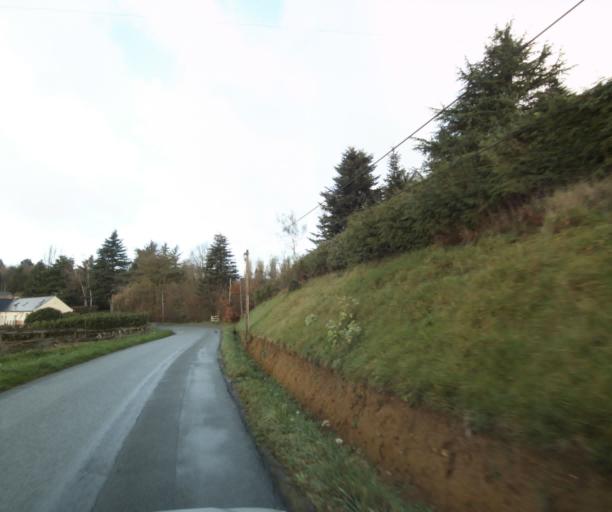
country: FR
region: Pays de la Loire
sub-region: Departement de la Sarthe
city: Sarge-les-le-Mans
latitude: 48.0078
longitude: 0.2373
